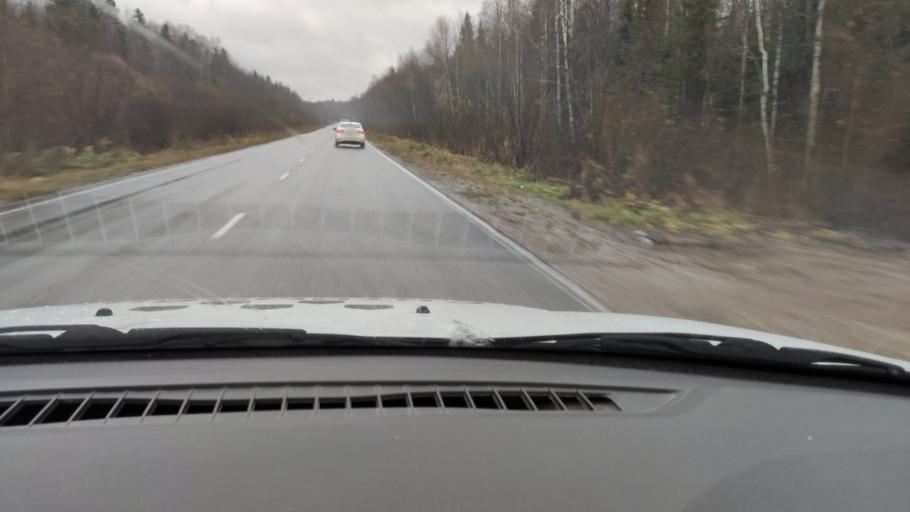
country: RU
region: Perm
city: Novyye Lyady
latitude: 58.0240
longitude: 56.6381
